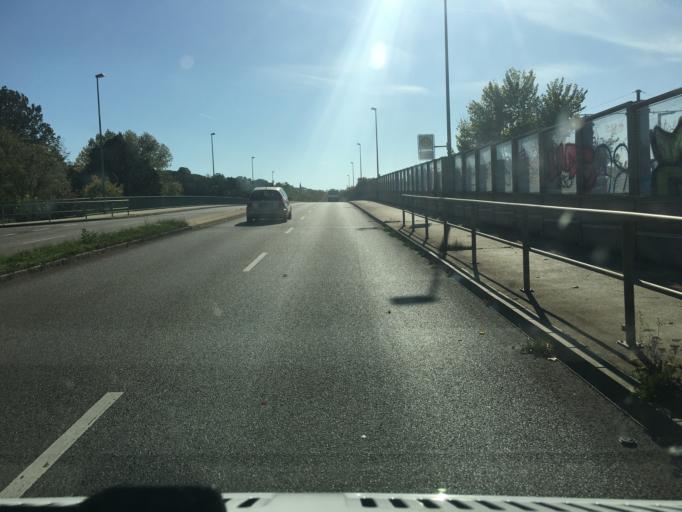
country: DE
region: Saxony
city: Zwickau
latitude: 50.7250
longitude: 12.5002
